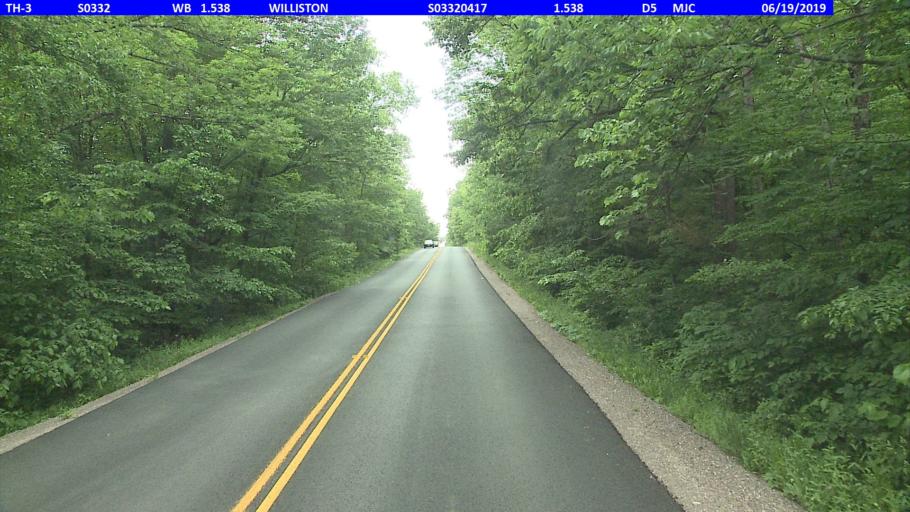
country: US
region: Vermont
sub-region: Chittenden County
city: Williston
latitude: 44.4194
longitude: -73.0942
